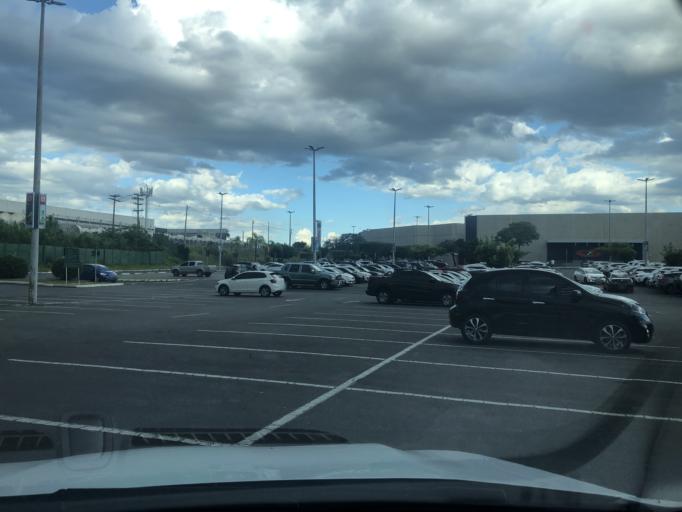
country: BR
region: Federal District
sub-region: Brasilia
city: Brasilia
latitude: -15.8322
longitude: -47.9573
